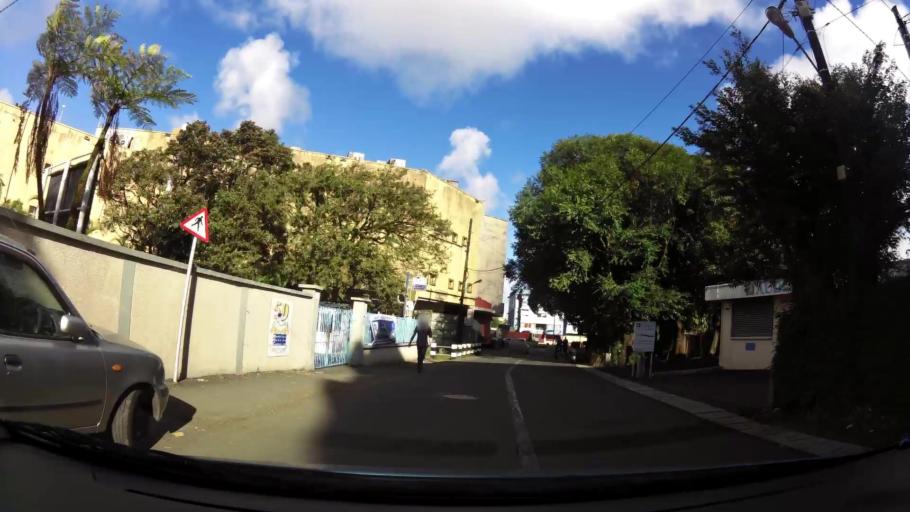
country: MU
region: Plaines Wilhems
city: Curepipe
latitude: -20.3189
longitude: 57.5291
